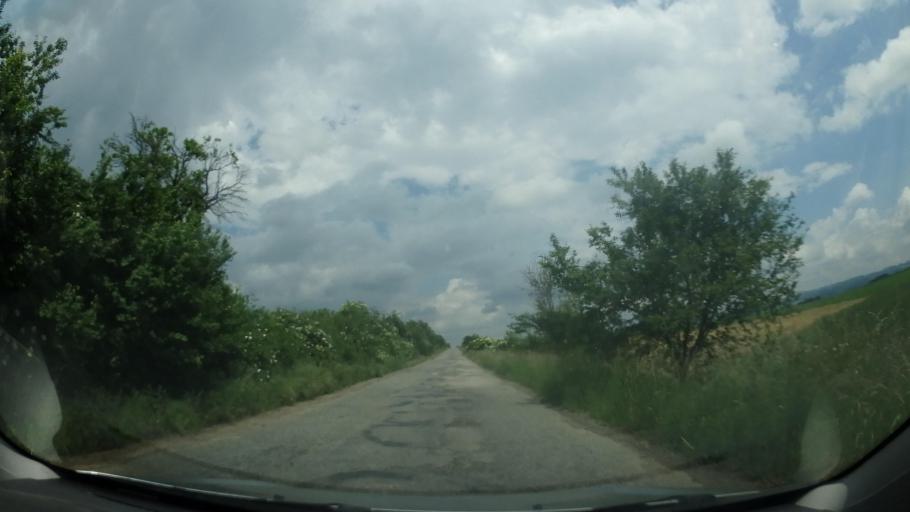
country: CZ
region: South Moravian
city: Boritov
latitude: 49.4329
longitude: 16.5935
